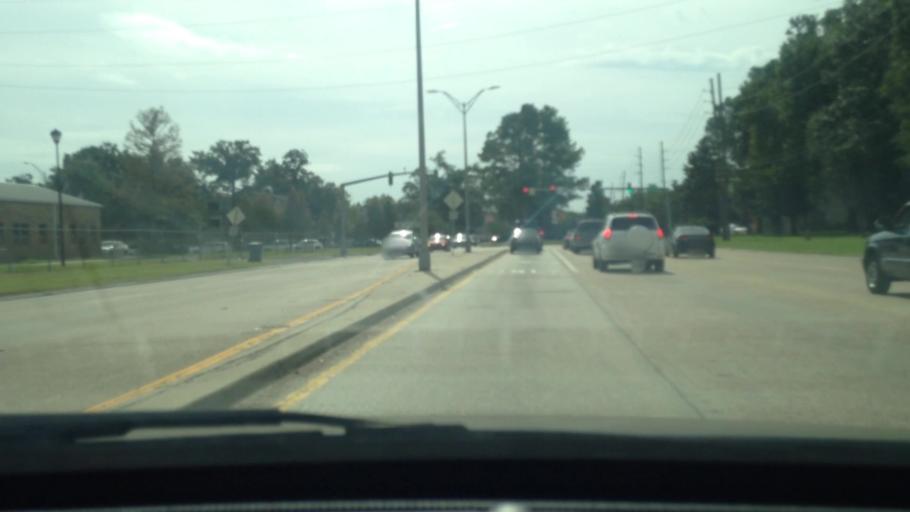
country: US
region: Louisiana
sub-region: Jefferson Parish
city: River Ridge
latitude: 29.9695
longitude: -90.2047
